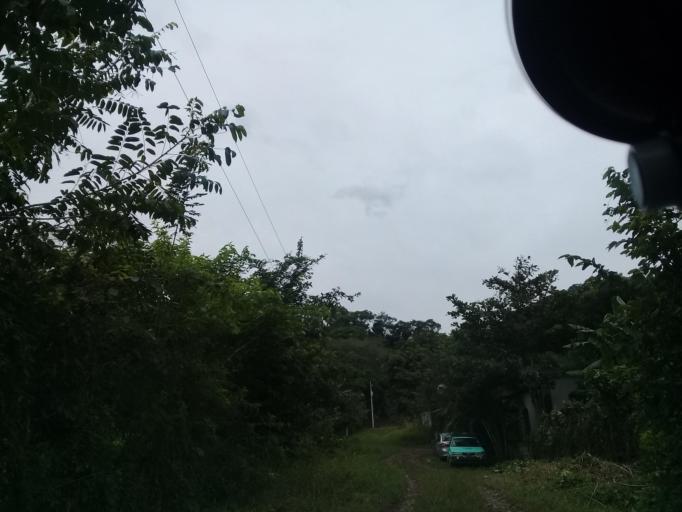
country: MX
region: Veracruz
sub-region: Chalma
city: San Pedro Coyutla
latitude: 21.2034
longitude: -98.3953
